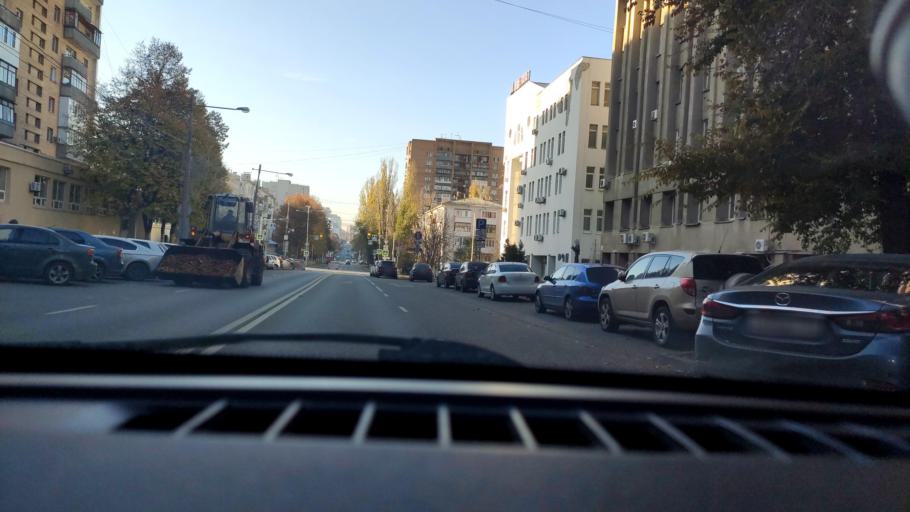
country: RU
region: Samara
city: Samara
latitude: 53.2091
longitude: 50.1258
